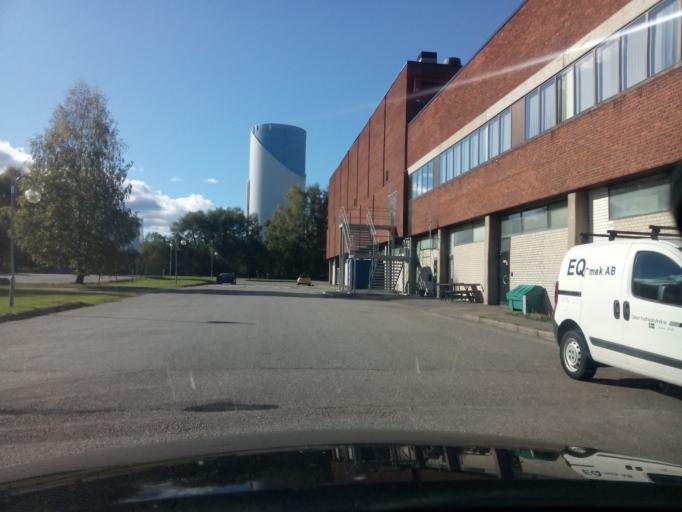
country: SE
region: Soedermanland
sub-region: Nykopings Kommun
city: Nykoping
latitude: 58.7441
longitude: 17.0047
